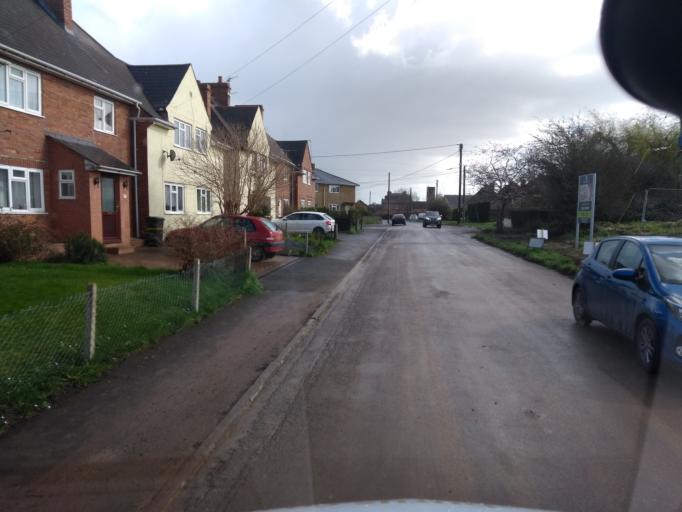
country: GB
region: England
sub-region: Somerset
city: Martock
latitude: 50.9772
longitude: -2.7709
